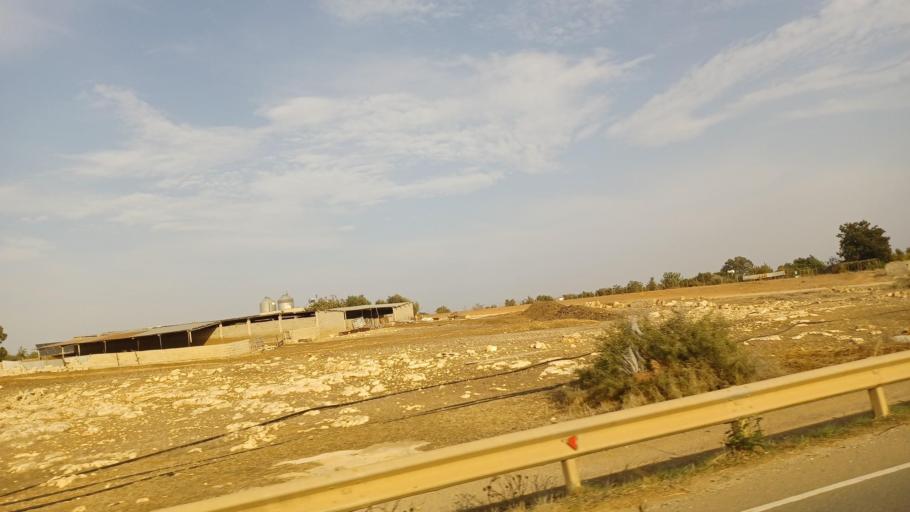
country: CY
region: Ammochostos
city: Frenaros
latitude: 35.0513
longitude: 33.9052
